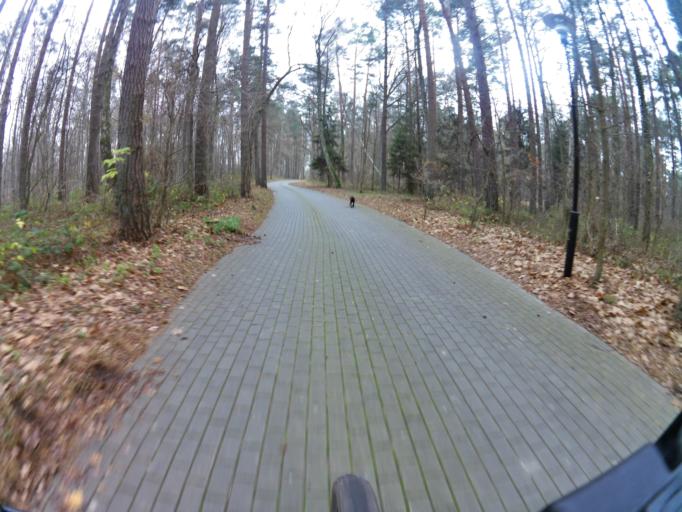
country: PL
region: West Pomeranian Voivodeship
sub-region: Powiat gryficki
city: Cerkwica
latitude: 54.0965
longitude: 15.1290
